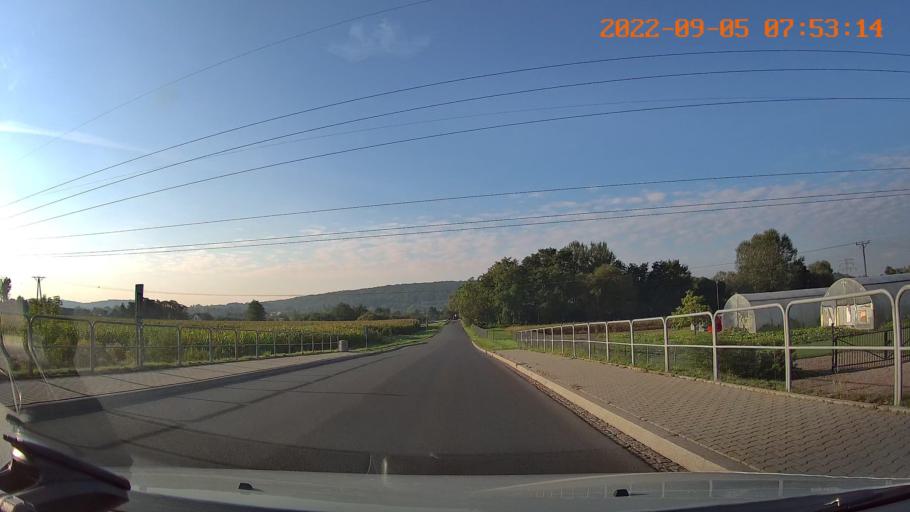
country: PL
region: Lesser Poland Voivodeship
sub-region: Powiat krakowski
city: Rzaska
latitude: 50.0797
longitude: 19.8485
